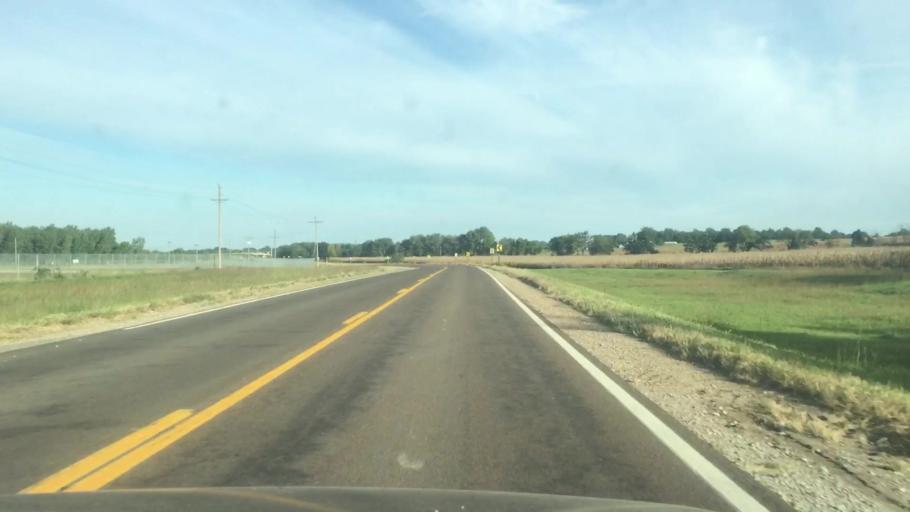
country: US
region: Nebraska
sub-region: Jefferson County
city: Fairbury
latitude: 40.1210
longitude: -97.1578
